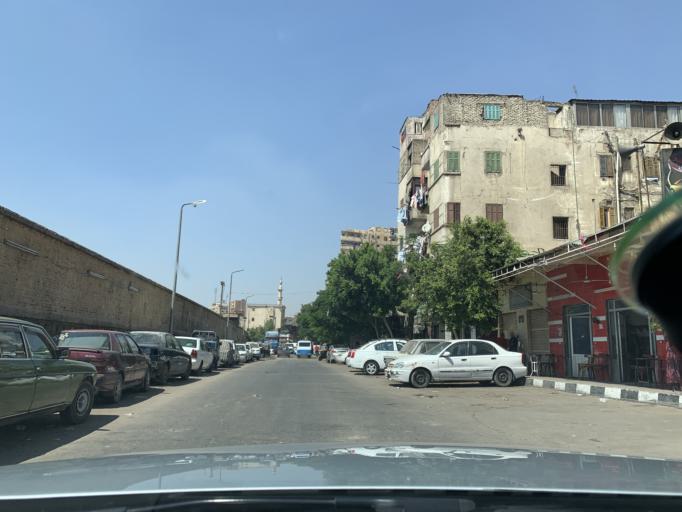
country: EG
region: Muhafazat al Qahirah
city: Cairo
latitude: 30.0689
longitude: 31.2545
